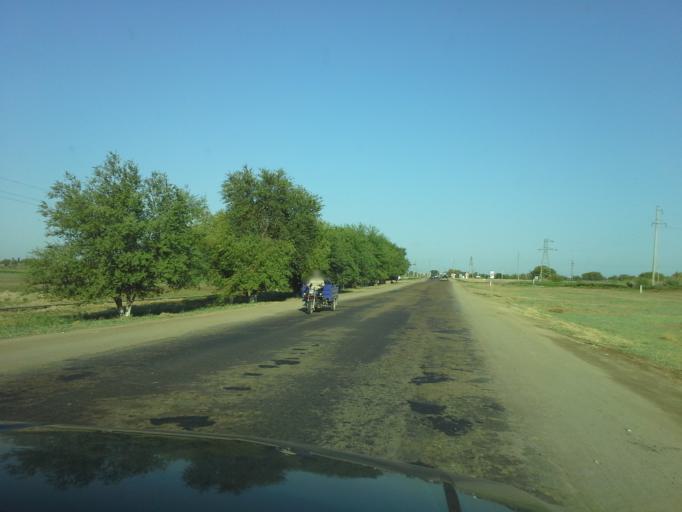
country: UZ
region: Karakalpakstan
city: Khujayli
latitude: 42.2297
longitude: 59.4673
